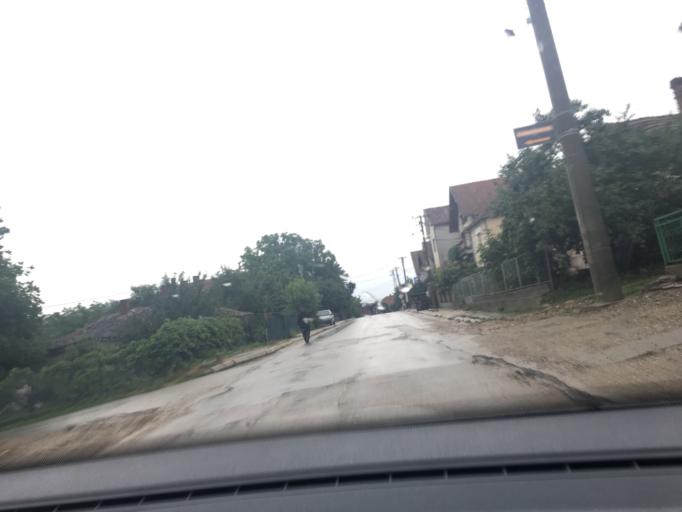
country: RS
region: Central Serbia
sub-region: Nisavski Okrug
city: Aleksinac
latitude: 43.5530
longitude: 21.7064
